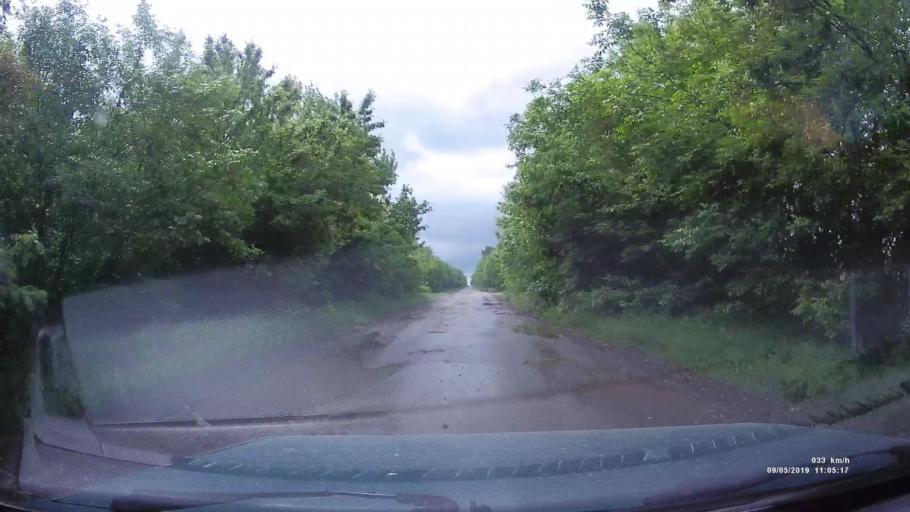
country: RU
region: Krasnodarskiy
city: Kanelovskaya
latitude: 46.8107
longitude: 39.2099
